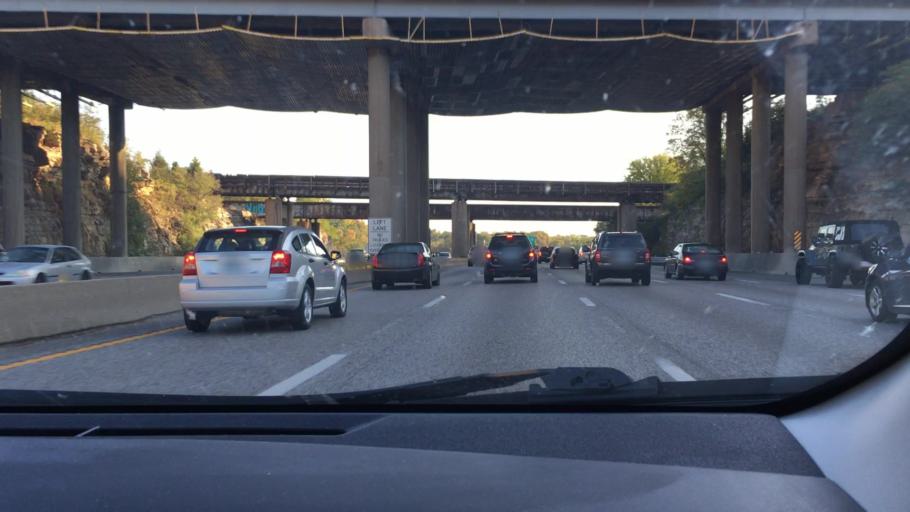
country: US
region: Missouri
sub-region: Saint Louis County
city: Des Peres
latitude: 38.5677
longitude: -90.4402
